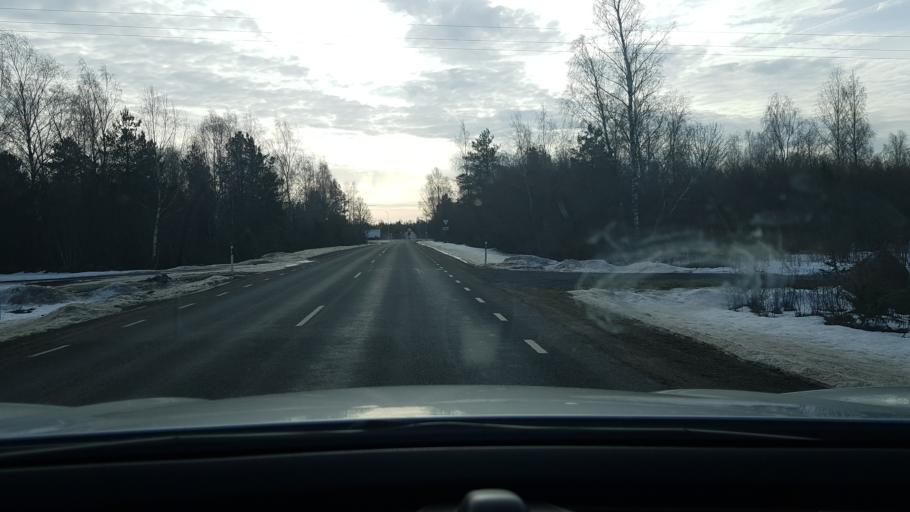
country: EE
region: Saare
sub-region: Kuressaare linn
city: Kuressaare
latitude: 58.2842
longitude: 22.5410
